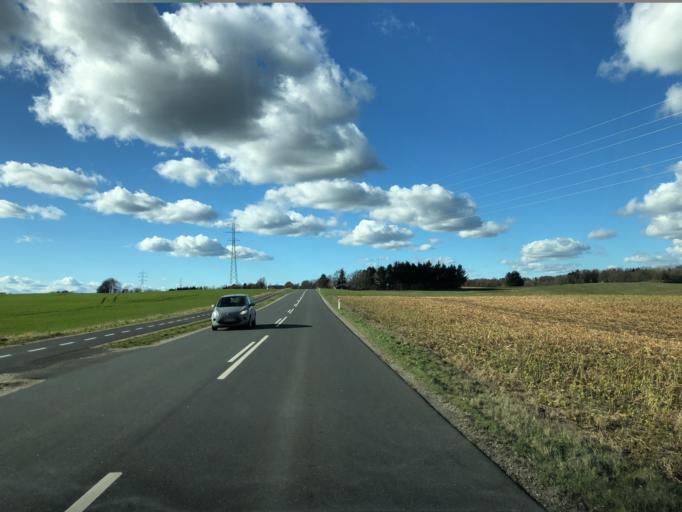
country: DK
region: Central Jutland
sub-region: Favrskov Kommune
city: Hinnerup
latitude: 56.2811
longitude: 10.0316
